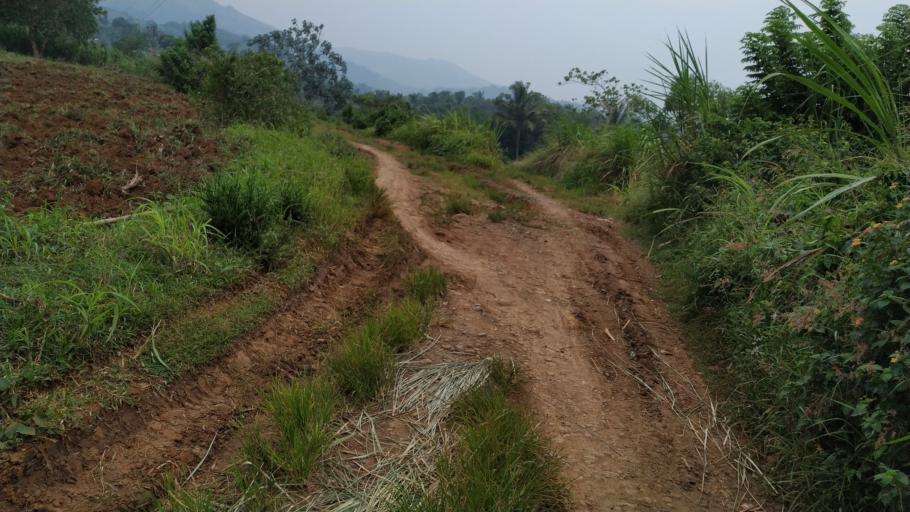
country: PH
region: Western Visayas
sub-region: Province of Negros Occidental
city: Quezon
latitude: 10.4231
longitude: 123.2386
